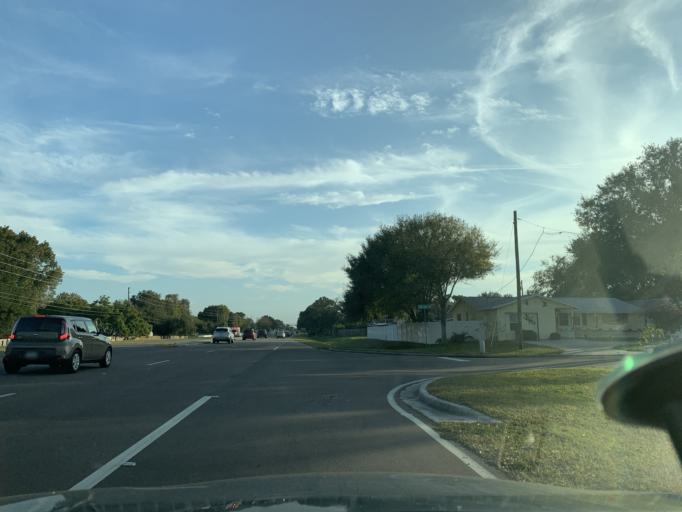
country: US
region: Florida
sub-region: Pinellas County
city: Ridgecrest
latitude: 27.8841
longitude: -82.7954
